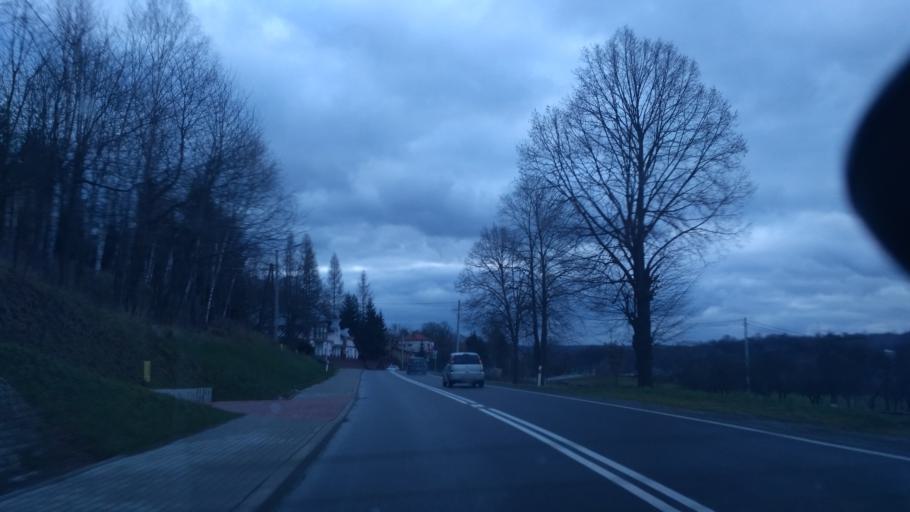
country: PL
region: Subcarpathian Voivodeship
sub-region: Powiat strzyzowski
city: Strzyzow
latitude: 49.8807
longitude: 21.8217
